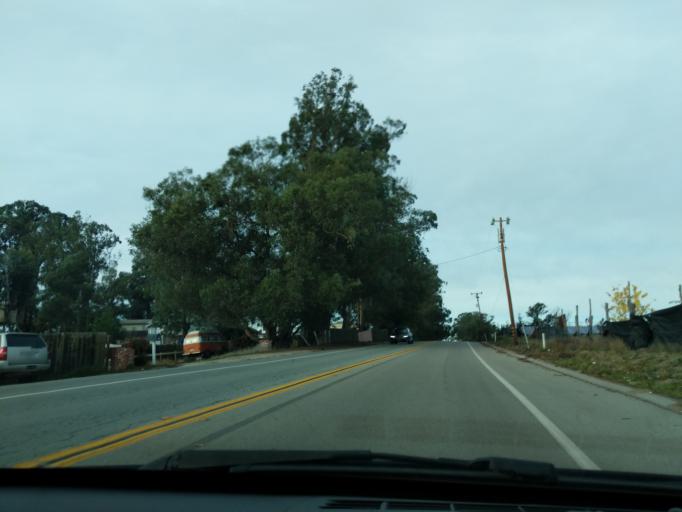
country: US
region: California
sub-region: San Luis Obispo County
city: Callender
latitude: 35.0410
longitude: -120.5680
